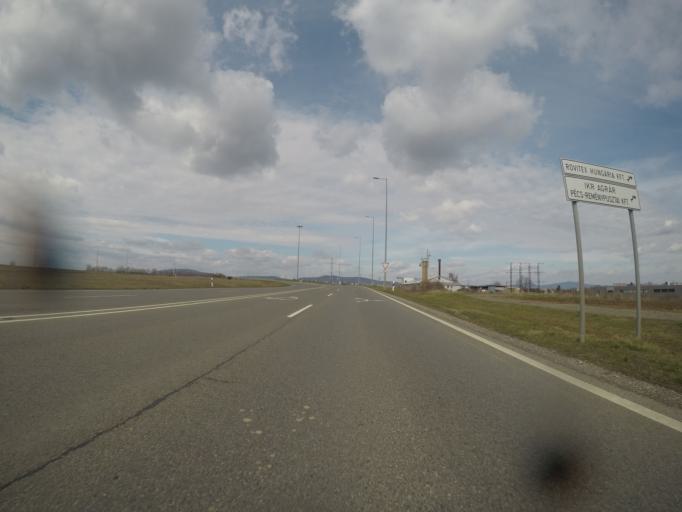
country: HU
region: Baranya
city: Kozarmisleny
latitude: 46.0180
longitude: 18.2347
